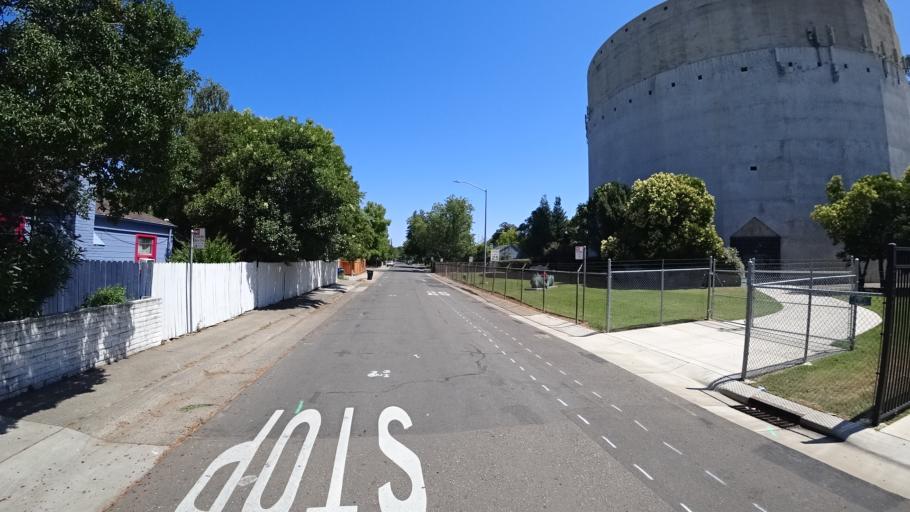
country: US
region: California
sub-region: Sacramento County
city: Sacramento
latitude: 38.5425
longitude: -121.4882
